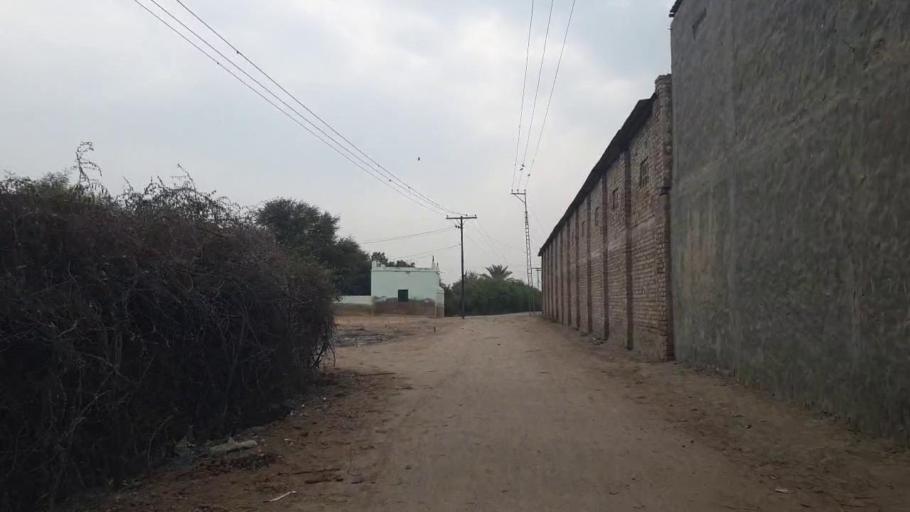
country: PK
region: Sindh
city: Shahdadpur
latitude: 25.9274
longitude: 68.6607
